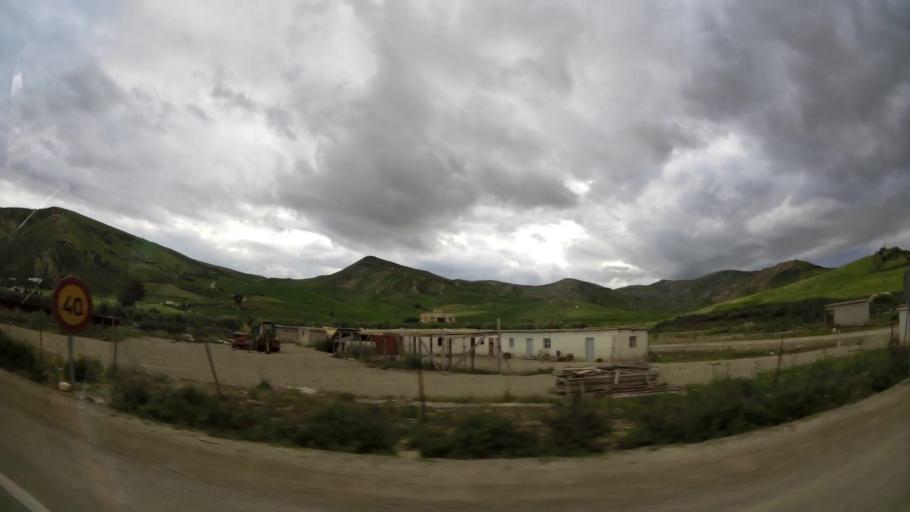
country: MA
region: Taza-Al Hoceima-Taounate
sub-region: Taza
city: Taza
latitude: 34.2923
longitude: -3.9685
